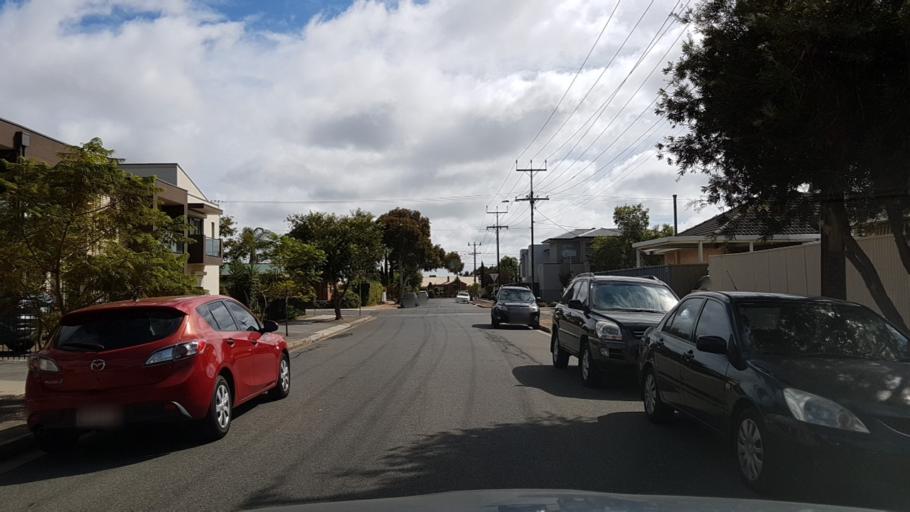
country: AU
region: South Australia
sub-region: Marion
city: Plympton Park
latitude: -34.9841
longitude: 138.5499
